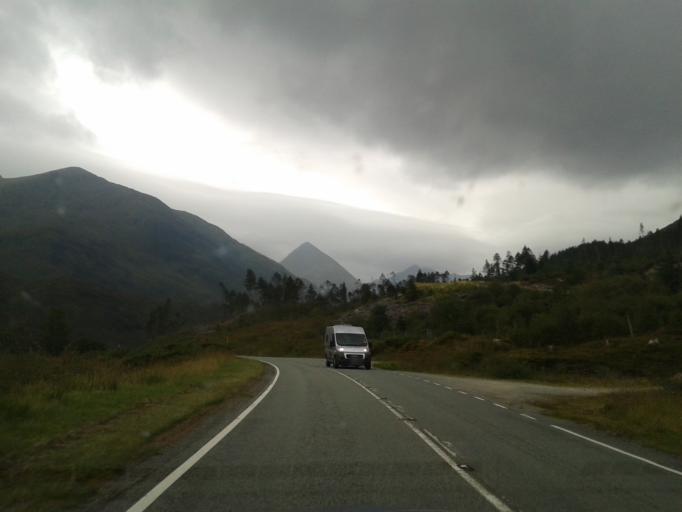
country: GB
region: Scotland
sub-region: Highland
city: Fort William
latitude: 57.1694
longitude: -5.3002
